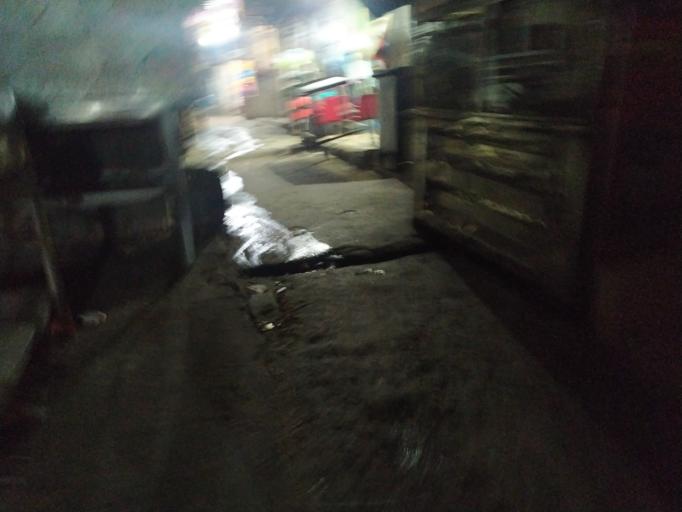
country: EG
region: Alexandria
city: Alexandria
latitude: 31.2129
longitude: 29.9245
